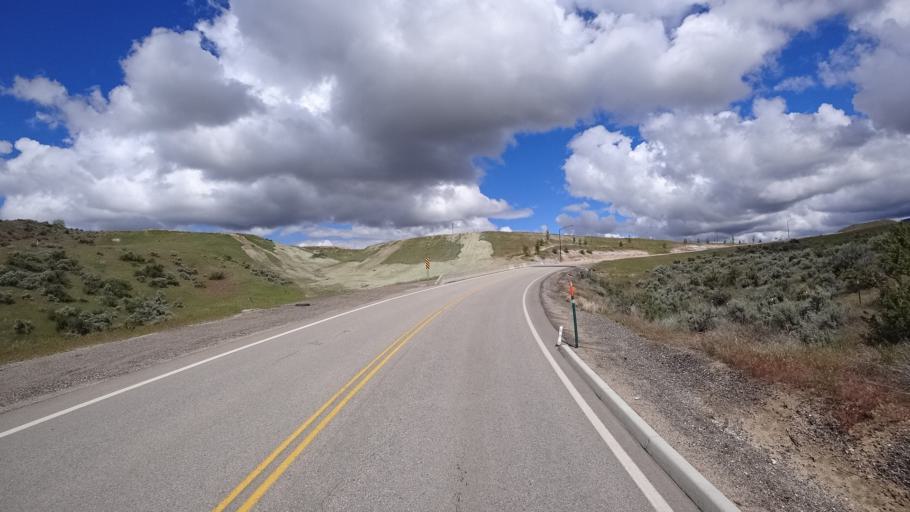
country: US
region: Idaho
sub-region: Ada County
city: Boise
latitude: 43.6627
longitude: -116.1917
